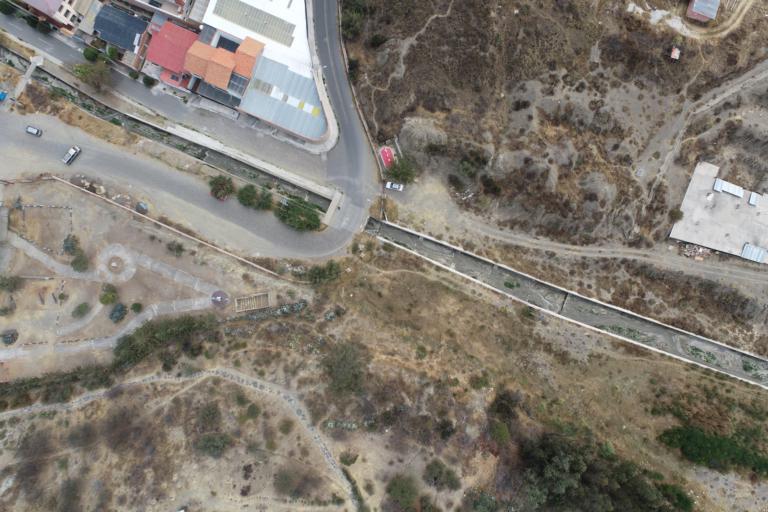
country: BO
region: La Paz
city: La Paz
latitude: -16.5372
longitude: -68.0693
